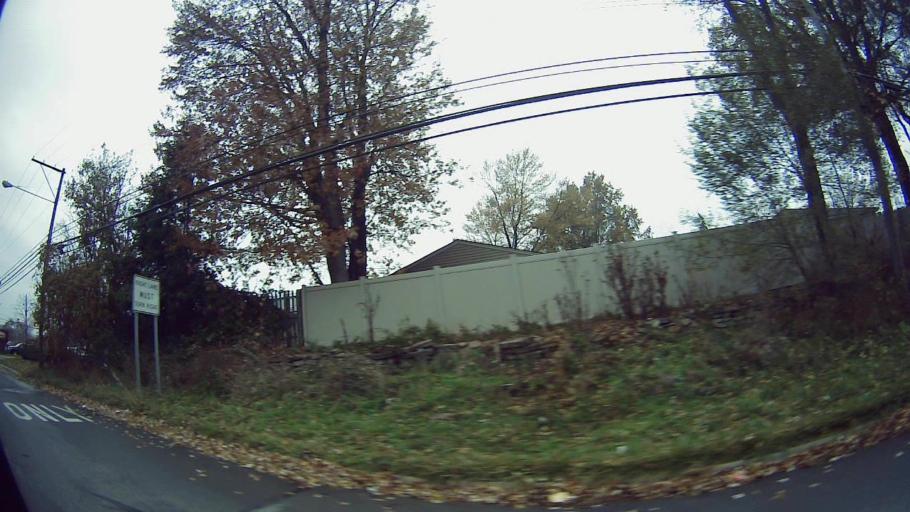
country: US
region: Michigan
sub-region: Wayne County
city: Dearborn Heights
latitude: 42.3423
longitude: -83.2737
